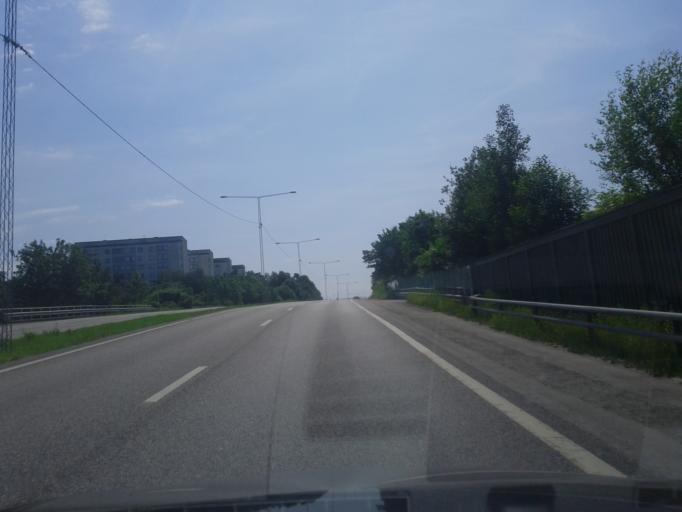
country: SE
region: Stockholm
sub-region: Huddinge Kommun
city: Huddinge
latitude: 59.2645
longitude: 18.0067
